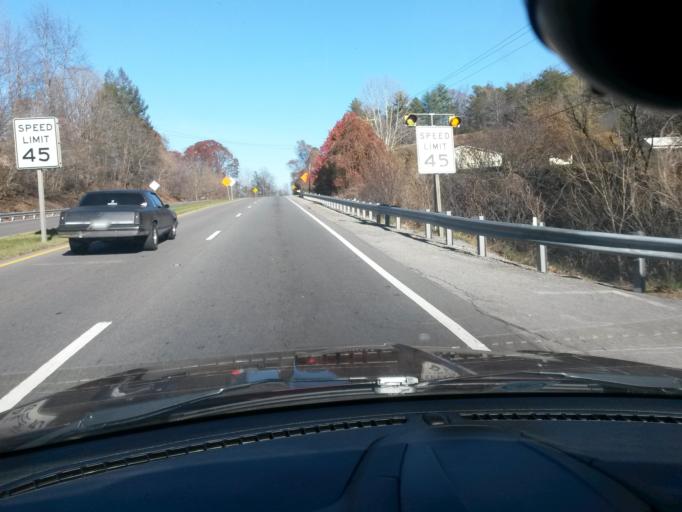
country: US
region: Virginia
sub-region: Roanoke County
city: Narrows
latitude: 37.1741
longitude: -79.9409
